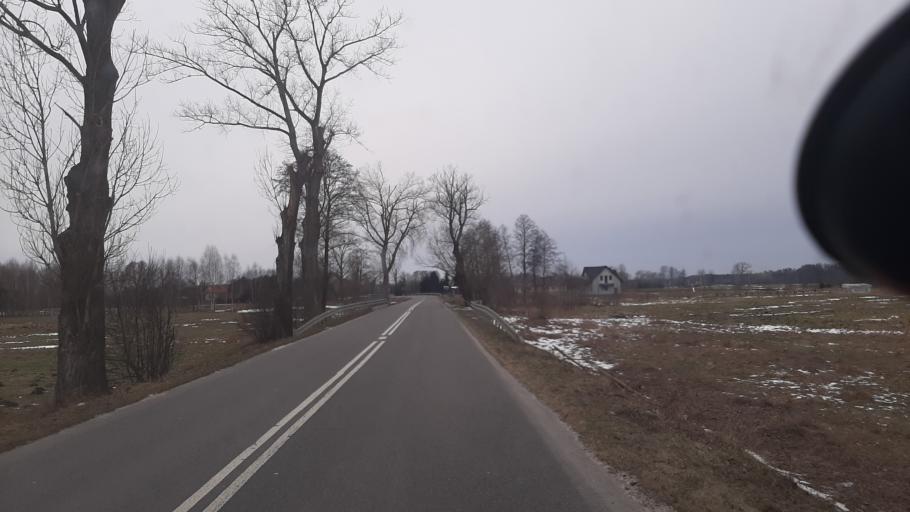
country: PL
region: Lublin Voivodeship
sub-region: Powiat lubartowski
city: Kamionka
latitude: 51.4873
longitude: 22.4451
